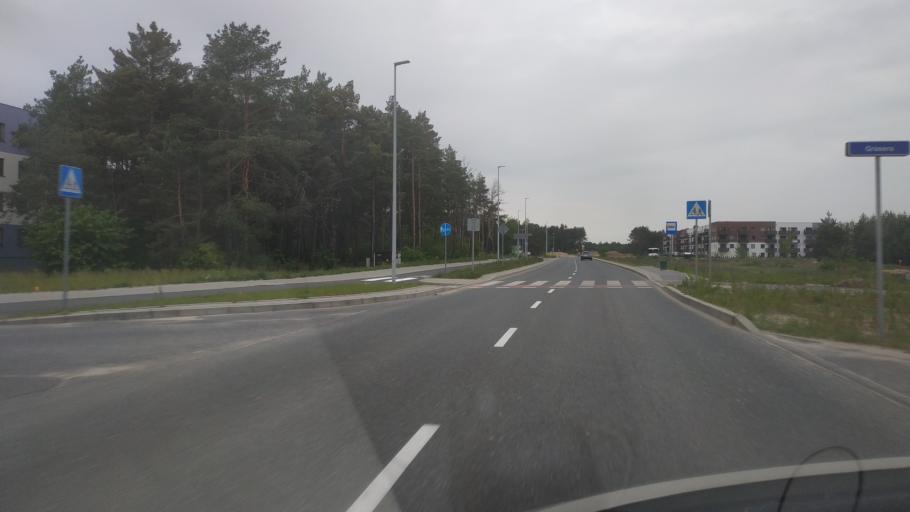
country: PL
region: Kujawsko-Pomorskie
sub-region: Torun
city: Torun
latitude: 53.0507
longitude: 18.6040
